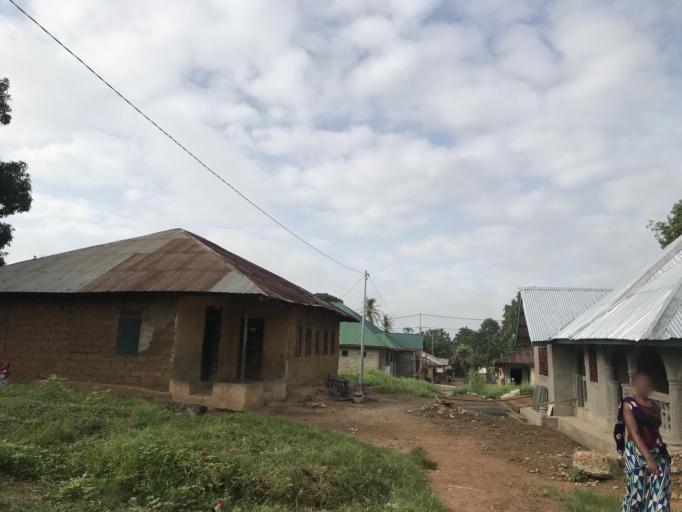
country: SL
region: Eastern Province
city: Pendembu
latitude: 8.0988
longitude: -10.6951
